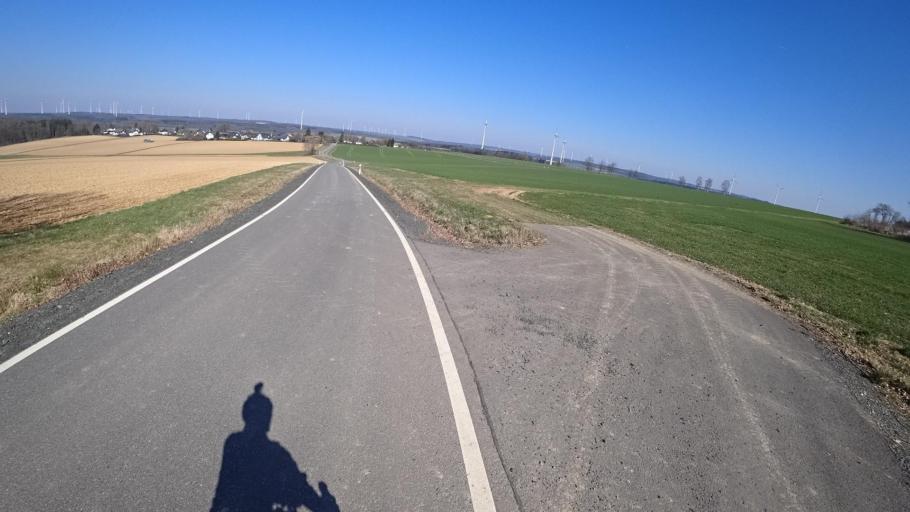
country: DE
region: Rheinland-Pfalz
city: Mutterschied
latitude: 49.9894
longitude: 7.5696
